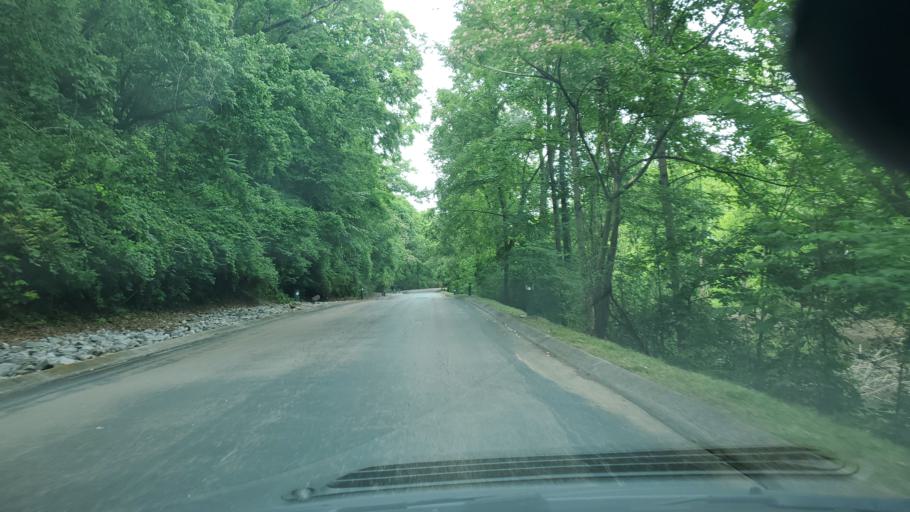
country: US
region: Tennessee
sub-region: Davidson County
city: Lakewood
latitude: 36.2179
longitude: -86.6826
